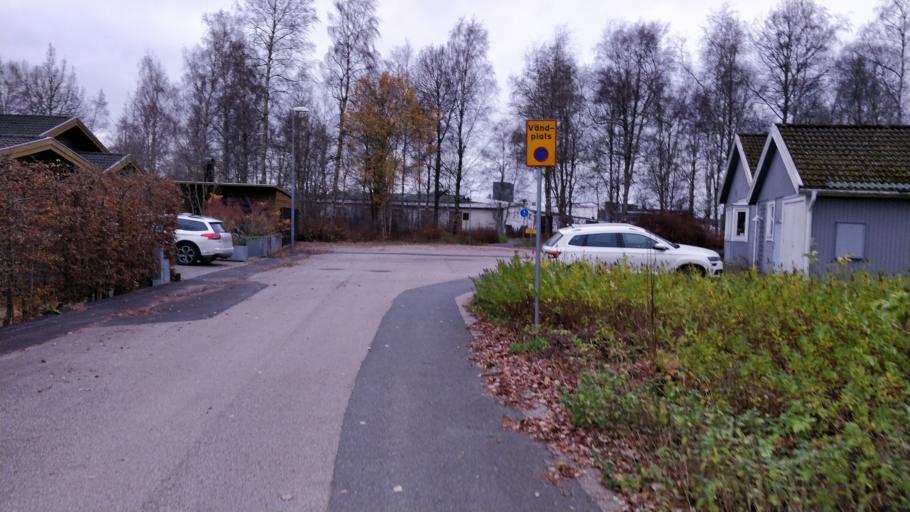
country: SE
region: Kronoberg
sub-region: Almhults Kommun
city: AElmhult
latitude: 56.5467
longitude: 14.1307
